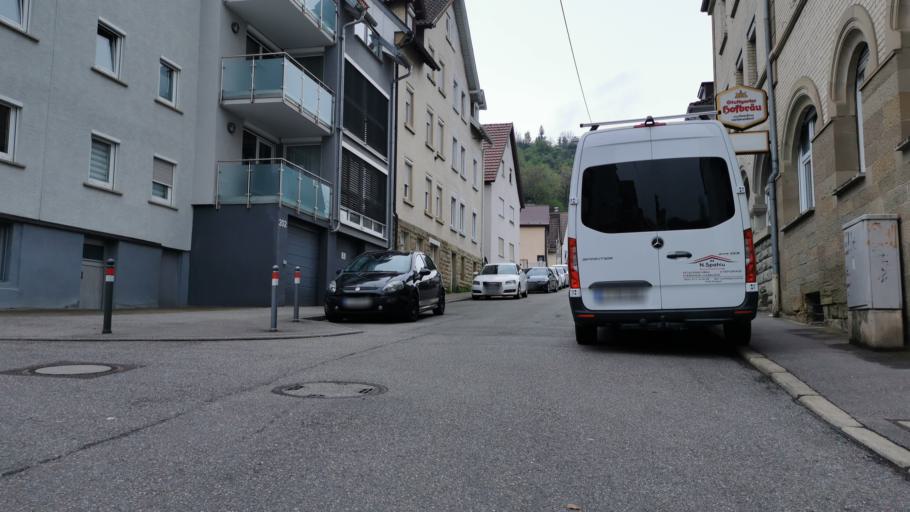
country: DE
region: Baden-Wuerttemberg
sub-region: Regierungsbezirk Stuttgart
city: Stuttgart Feuerbach
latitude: 48.8055
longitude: 9.1596
